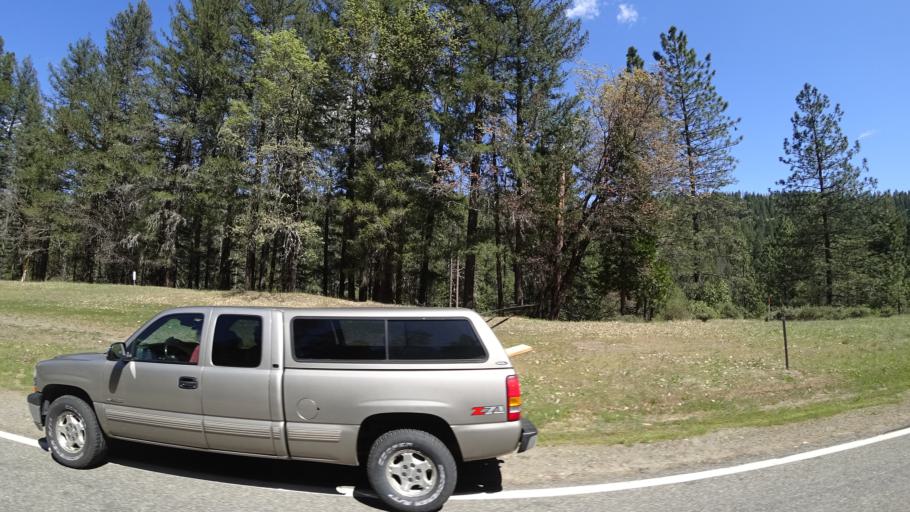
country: US
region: California
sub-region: Trinity County
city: Weaverville
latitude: 40.7533
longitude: -122.8869
